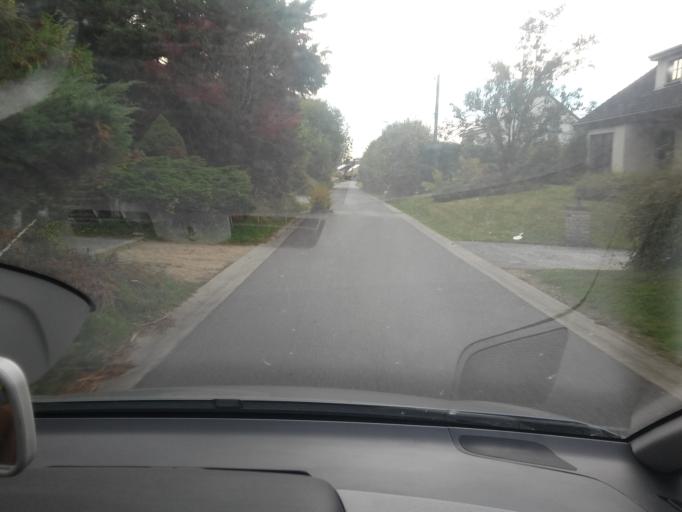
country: BE
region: Wallonia
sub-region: Province du Luxembourg
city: Attert
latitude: 49.7128
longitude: 5.7358
